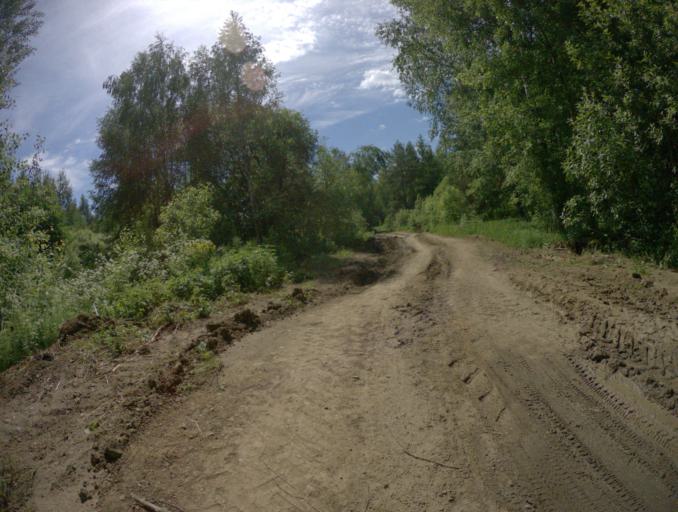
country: RU
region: Vladimir
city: Stavrovo
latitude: 56.3196
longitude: 40.0846
